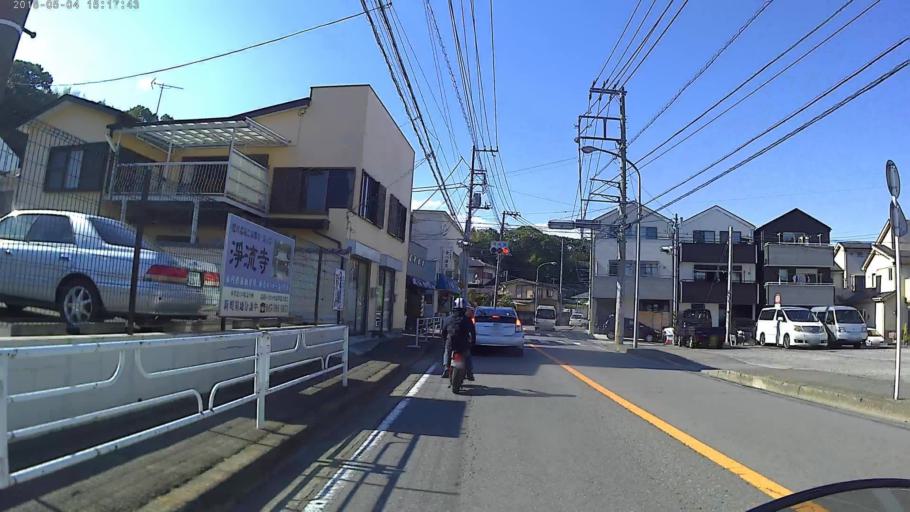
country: JP
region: Kanagawa
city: Yokohama
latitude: 35.5368
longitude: 139.6112
